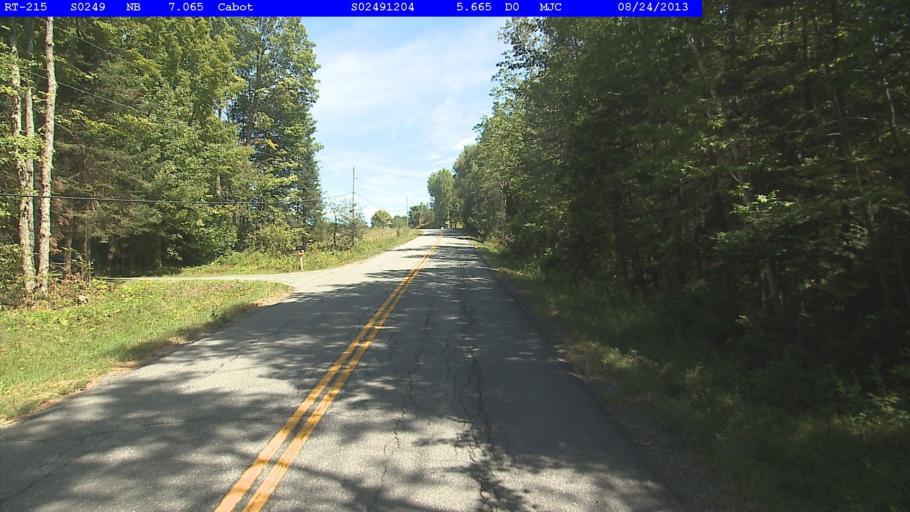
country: US
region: Vermont
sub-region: Caledonia County
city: Hardwick
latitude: 44.4336
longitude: -72.2860
